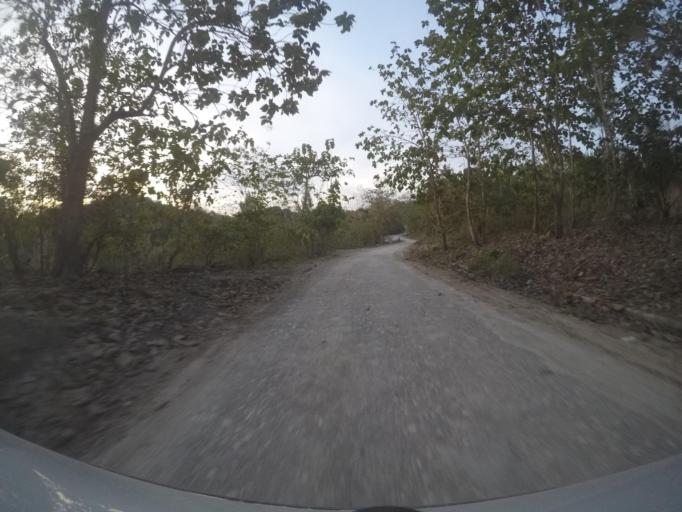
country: TL
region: Viqueque
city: Viqueque
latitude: -8.8899
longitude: 126.3863
